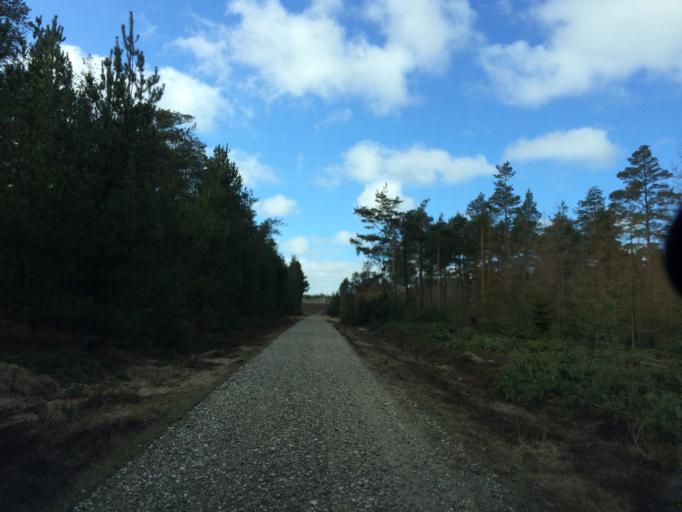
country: DK
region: Central Jutland
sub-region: Holstebro Kommune
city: Ulfborg
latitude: 56.2821
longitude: 8.4180
